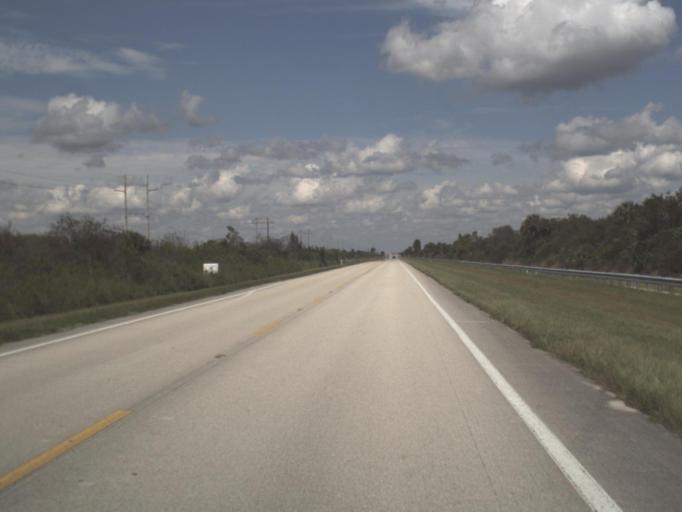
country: US
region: Florida
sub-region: Collier County
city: Orangetree
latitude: 26.1310
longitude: -81.3449
